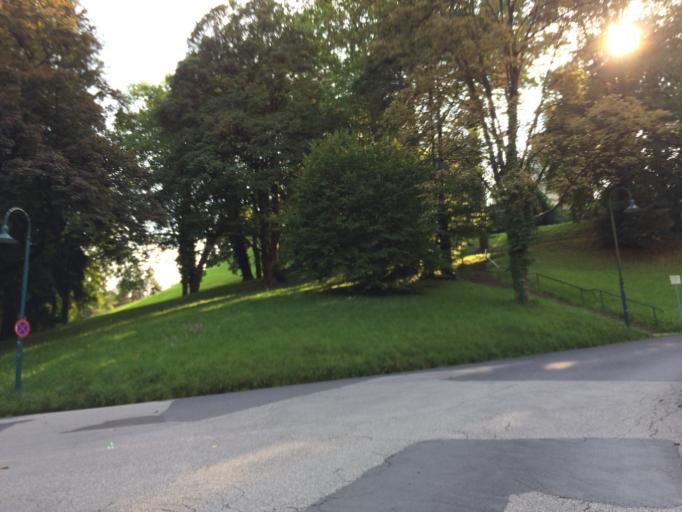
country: AT
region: Upper Austria
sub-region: Linz Stadt
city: Linz
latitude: 48.2970
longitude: 14.2830
